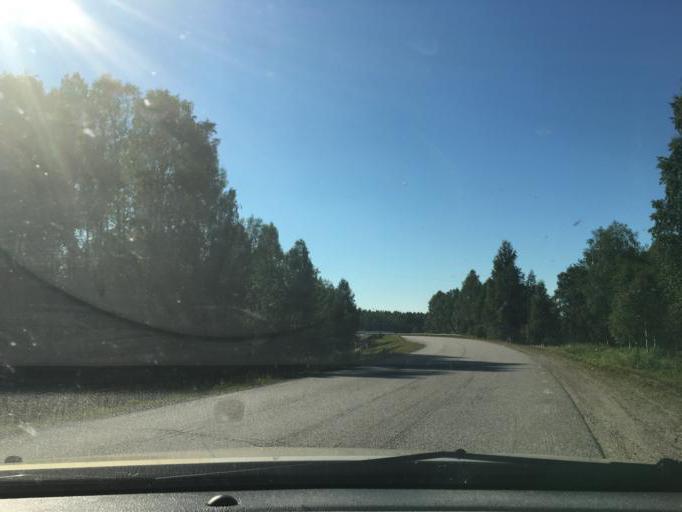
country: SE
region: Norrbotten
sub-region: Kalix Kommun
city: Toere
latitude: 66.0745
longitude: 22.7390
